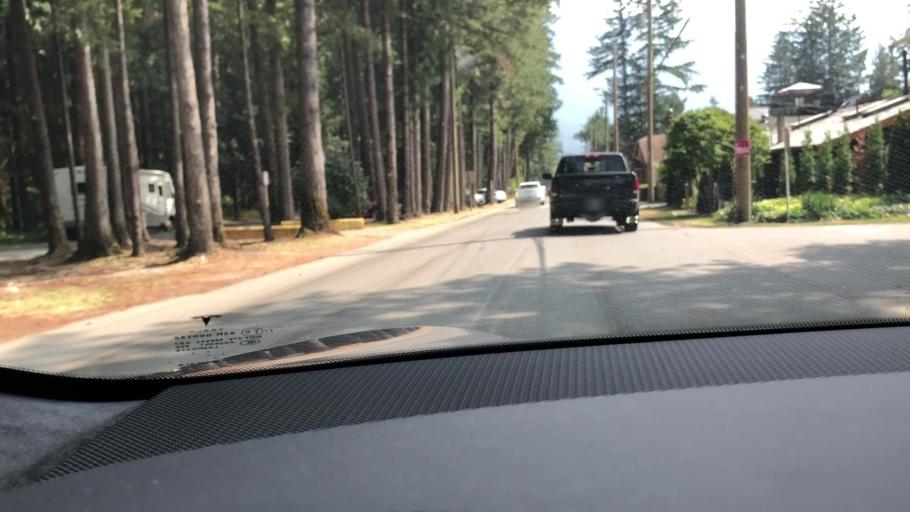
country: CA
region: British Columbia
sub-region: Fraser Valley Regional District
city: Chilliwack
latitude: 49.0703
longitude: -121.9763
